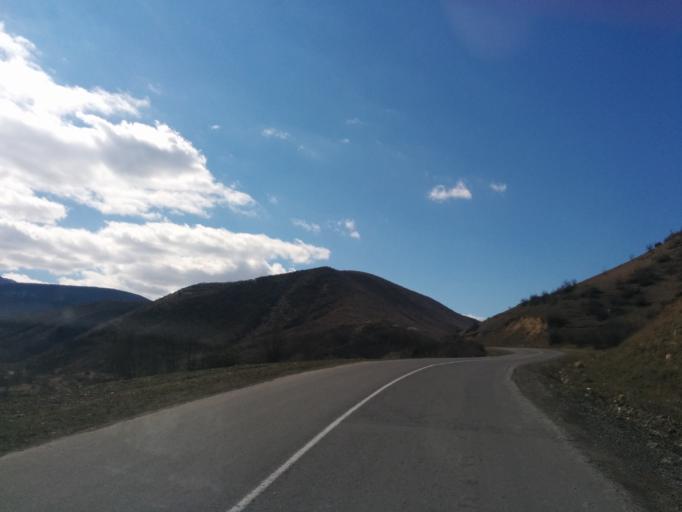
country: GE
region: Mtskheta-Mtianeti
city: Mtskheta
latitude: 41.8381
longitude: 44.5733
